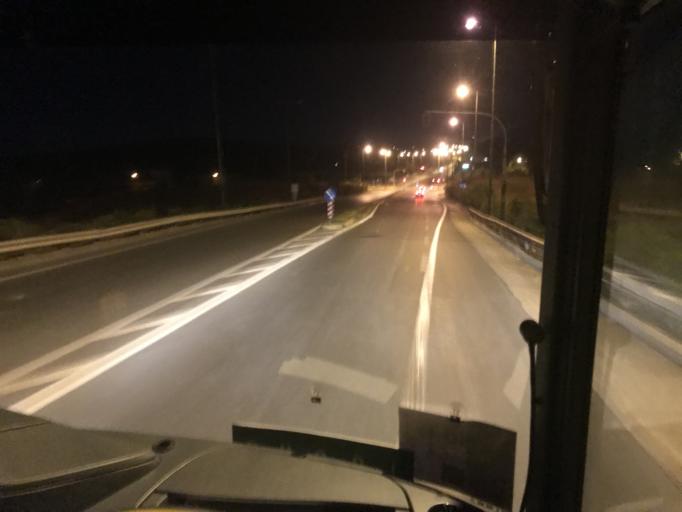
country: GR
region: Crete
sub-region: Nomos Irakleiou
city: Skalanion
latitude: 35.2809
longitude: 25.1804
